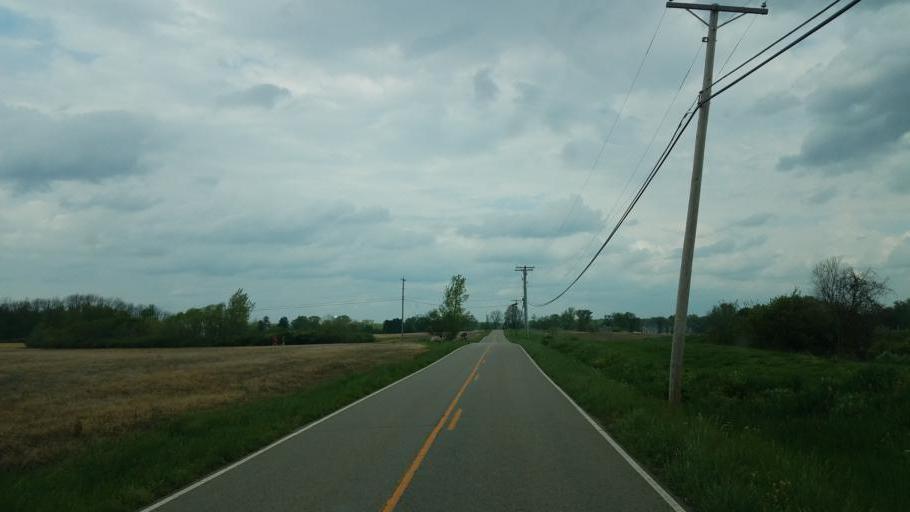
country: US
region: Ohio
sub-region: Licking County
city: Harbor Hills
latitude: 39.9206
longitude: -82.4400
